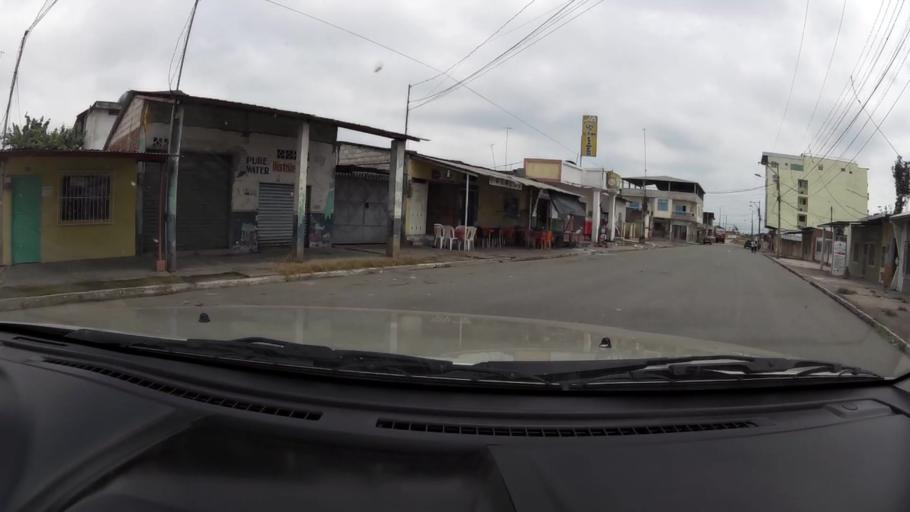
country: EC
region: El Oro
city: Pasaje
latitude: -3.2460
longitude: -79.8304
